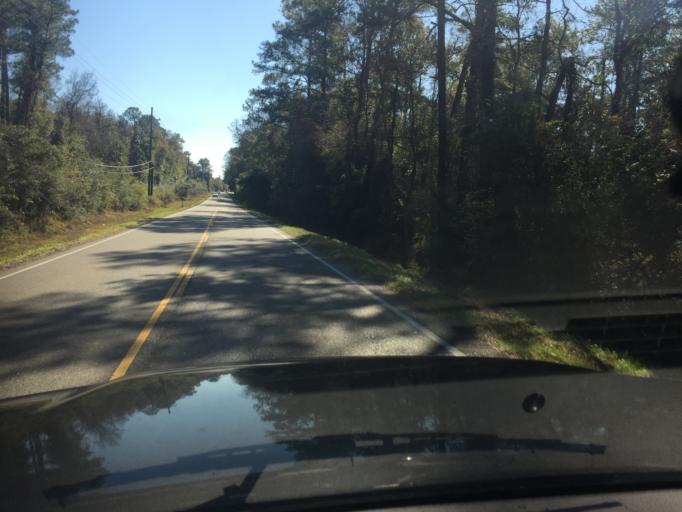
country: US
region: Louisiana
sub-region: Saint Tammany Parish
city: Slidell
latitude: 30.3074
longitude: -89.7286
